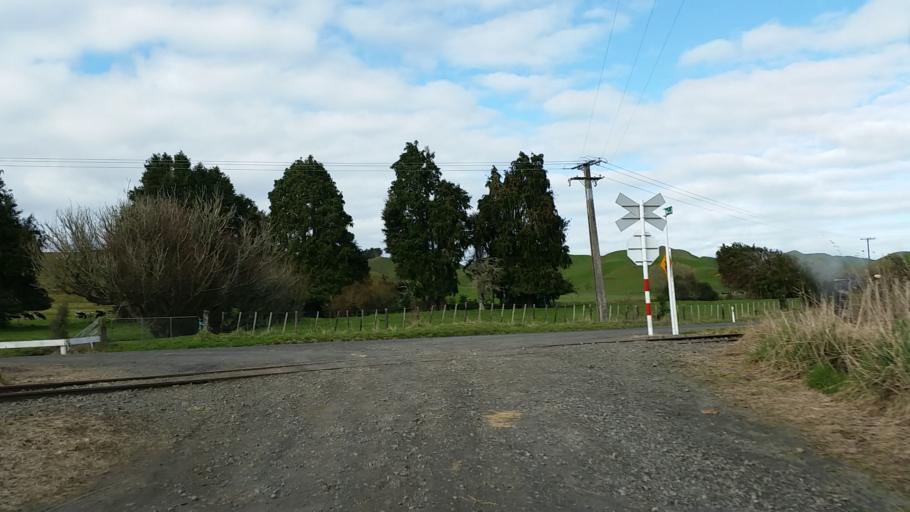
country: NZ
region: Taranaki
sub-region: South Taranaki District
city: Eltham
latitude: -39.2343
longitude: 174.5203
